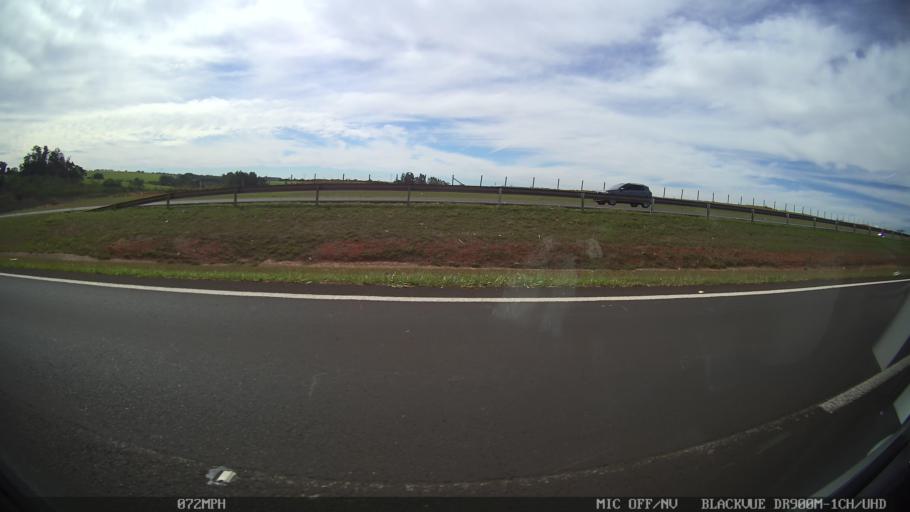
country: BR
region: Sao Paulo
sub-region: Taquaritinga
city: Taquaritinga
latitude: -21.5236
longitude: -48.5293
